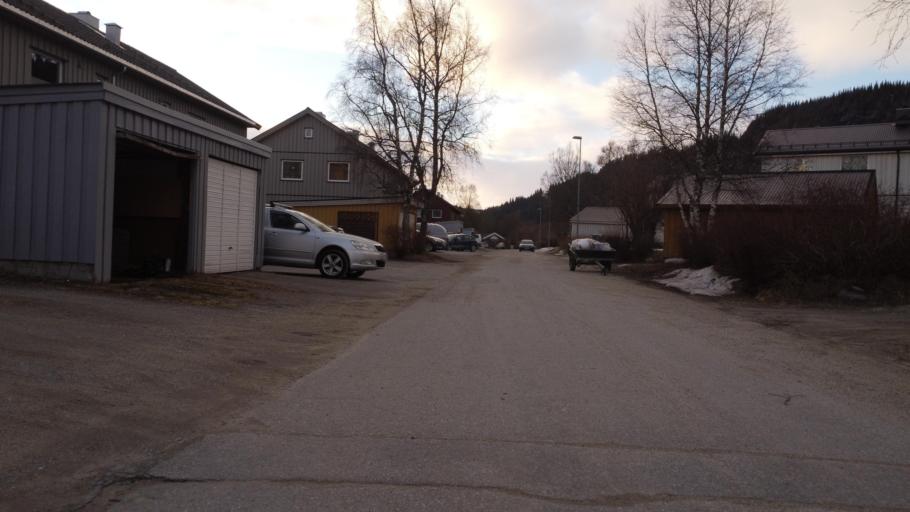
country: NO
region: Nordland
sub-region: Rana
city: Mo i Rana
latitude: 66.3258
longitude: 14.1715
